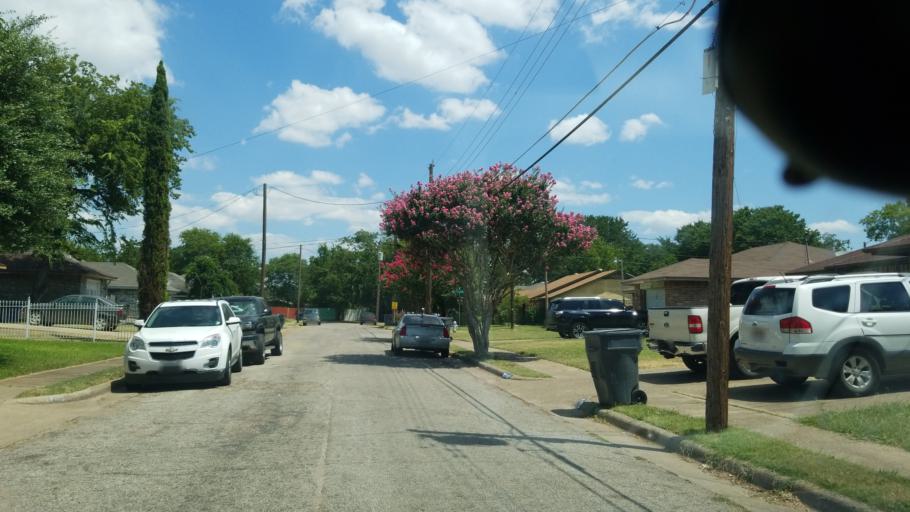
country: US
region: Texas
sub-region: Dallas County
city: Cockrell Hill
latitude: 32.7289
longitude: -96.8390
